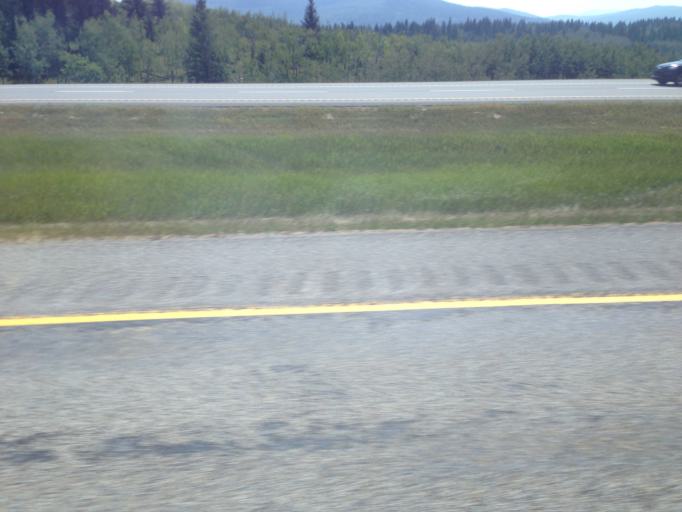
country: CA
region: Alberta
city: Cochrane
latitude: 51.1414
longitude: -114.8845
